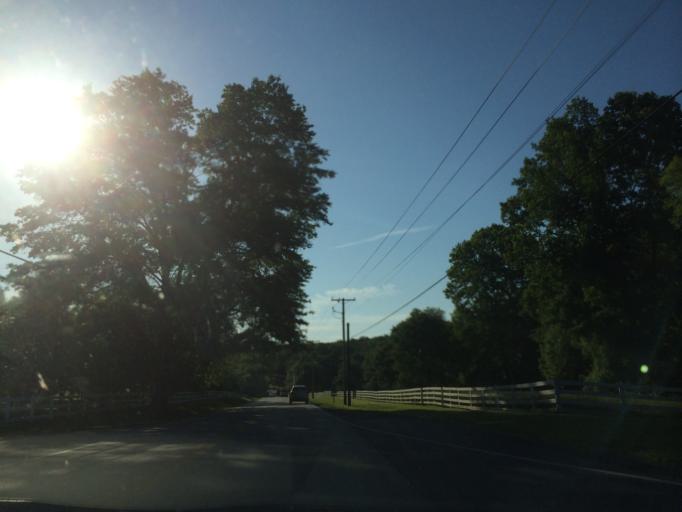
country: US
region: Maryland
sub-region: Howard County
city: Highland
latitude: 39.2573
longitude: -76.9665
